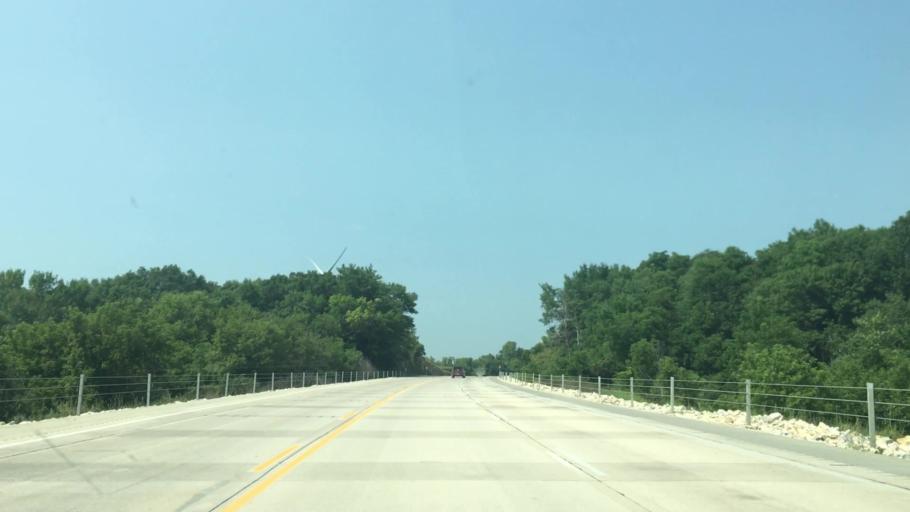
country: US
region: Iowa
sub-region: Winneshiek County
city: Decorah
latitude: 43.3030
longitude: -91.8144
